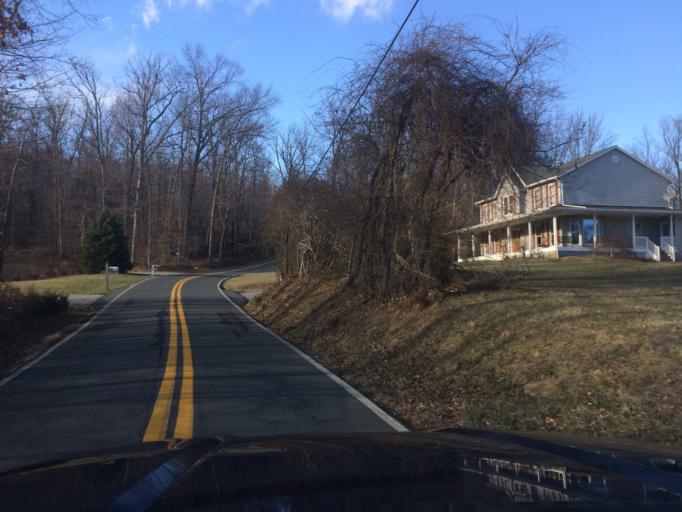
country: US
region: Maryland
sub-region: Carroll County
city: Eldersburg
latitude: 39.3681
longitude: -76.8996
